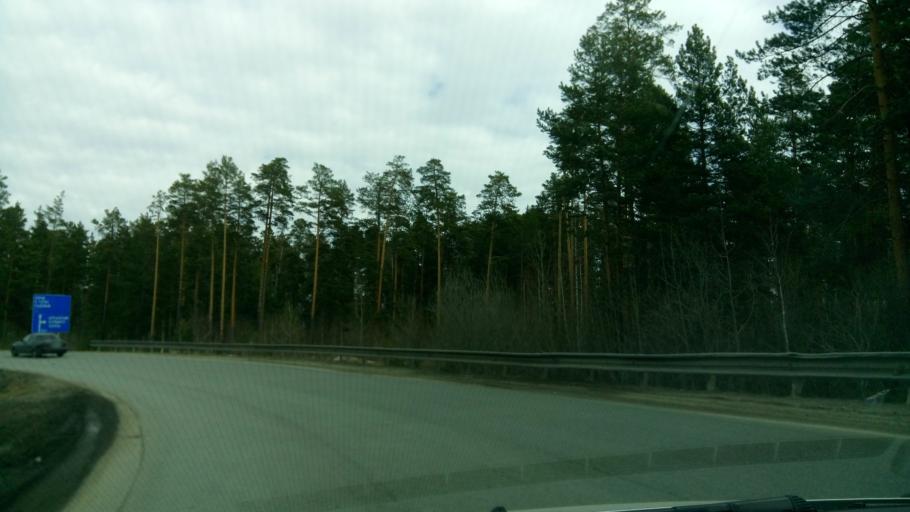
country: RU
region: Sverdlovsk
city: Verkhnyaya Pyshma
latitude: 56.9388
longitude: 60.6353
